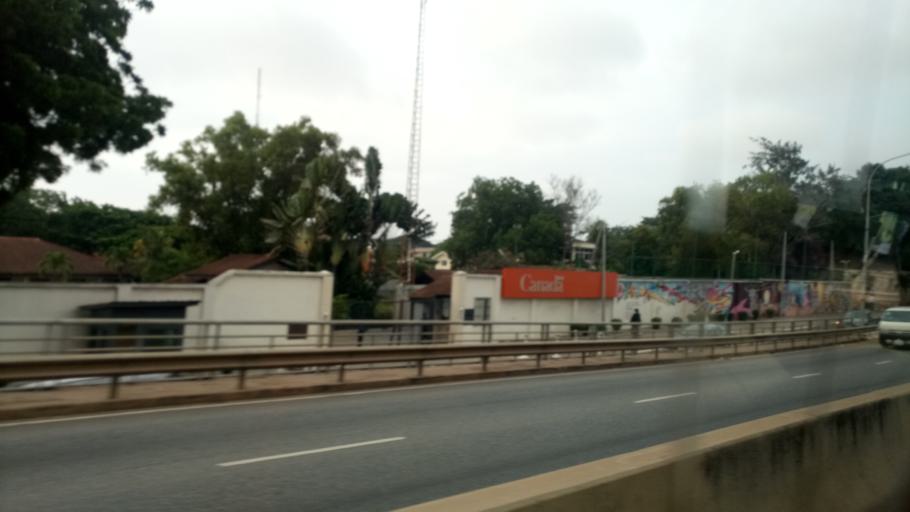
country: GH
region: Greater Accra
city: Accra
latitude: 5.5713
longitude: -0.1909
